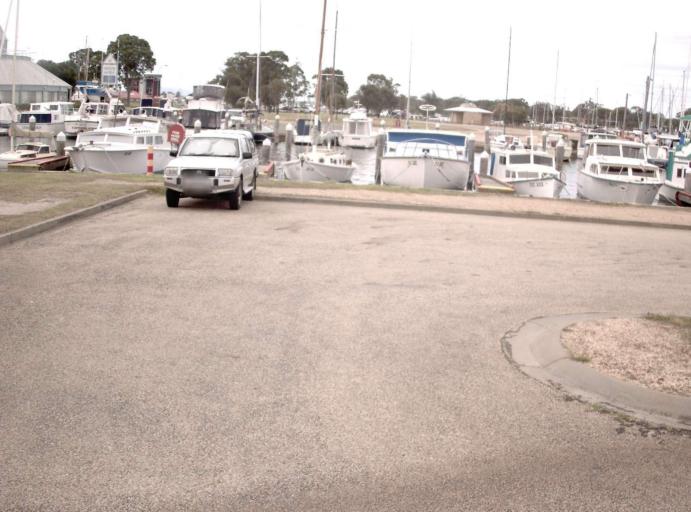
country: AU
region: Victoria
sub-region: East Gippsland
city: Bairnsdale
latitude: -37.9176
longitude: 147.7261
